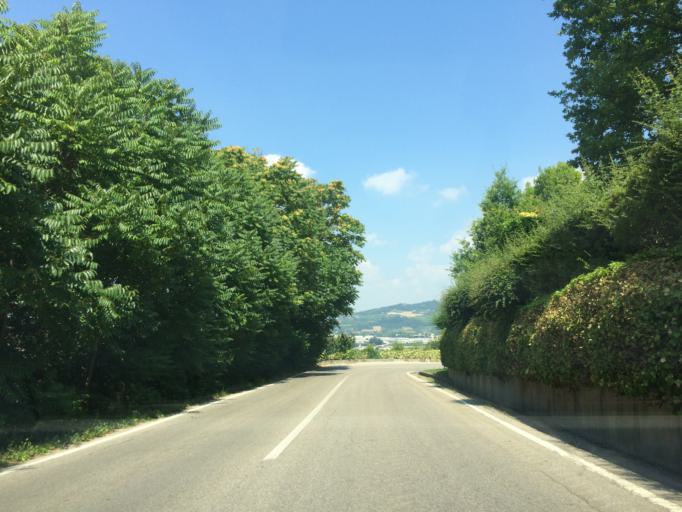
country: IT
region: Piedmont
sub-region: Provincia di Cuneo
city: Alba
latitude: 44.6966
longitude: 8.0470
